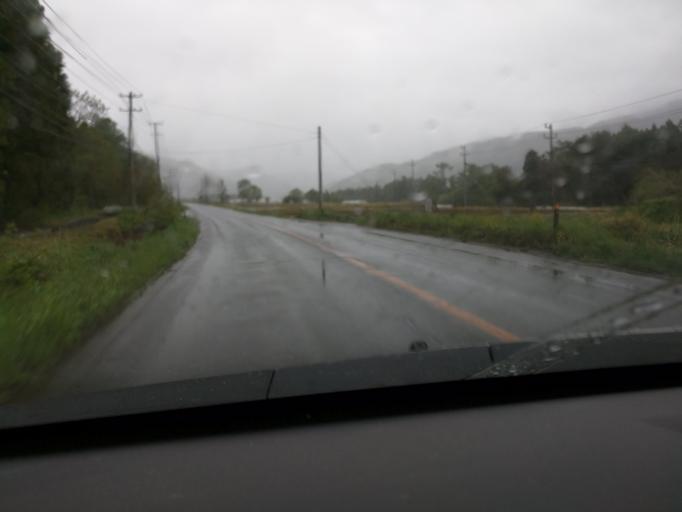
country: JP
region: Fukushima
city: Inawashiro
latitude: 37.5842
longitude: 140.1241
